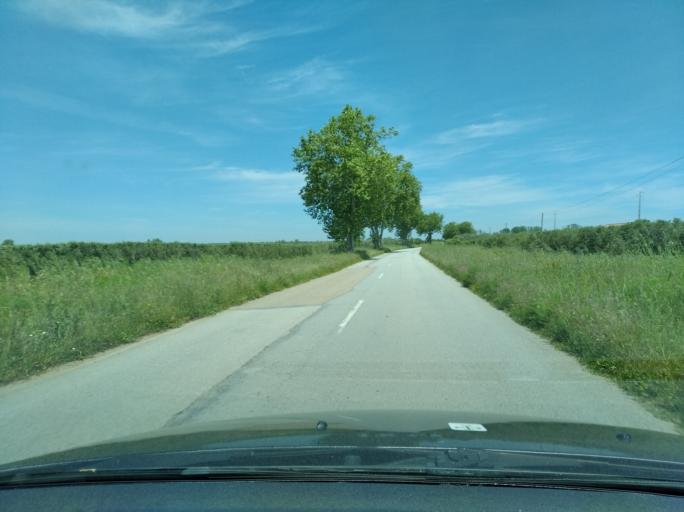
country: PT
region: Portalegre
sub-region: Avis
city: Avis
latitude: 39.0775
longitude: -7.8810
